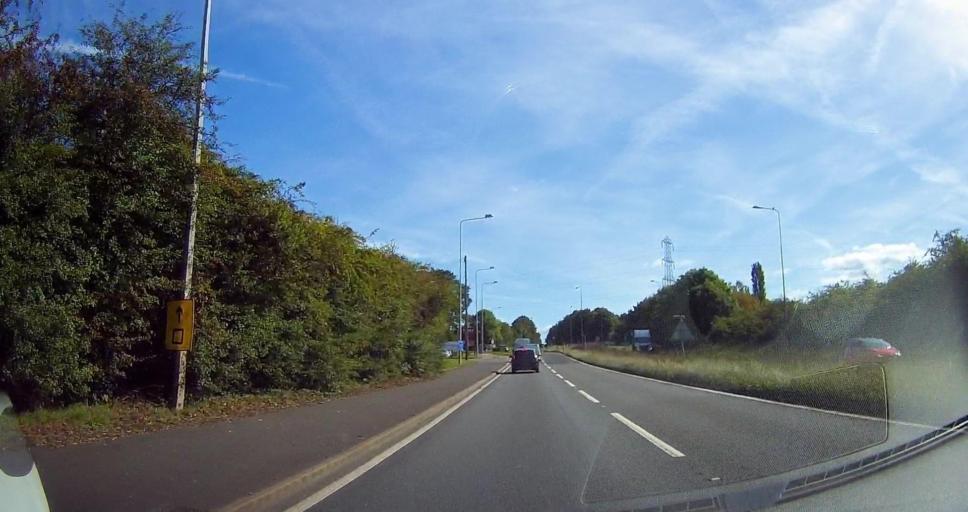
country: GB
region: England
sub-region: Staffordshire
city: Norton Canes
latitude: 52.6610
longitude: -1.9755
